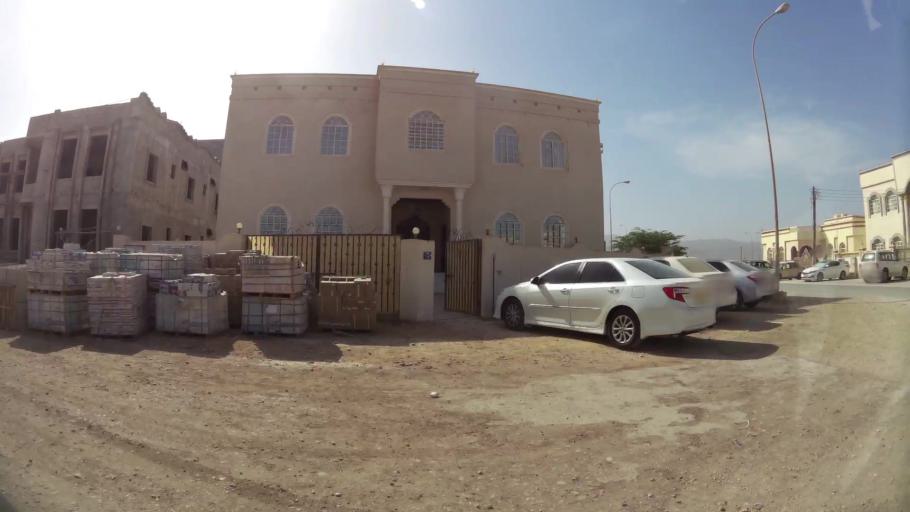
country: OM
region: Zufar
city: Salalah
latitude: 17.0096
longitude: 54.0027
